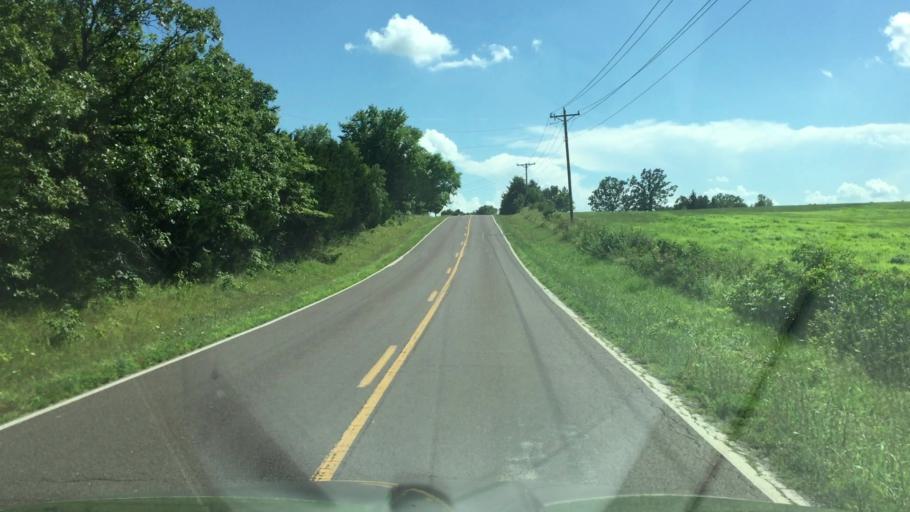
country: US
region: Missouri
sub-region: Miller County
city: Tuscumbia
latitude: 38.1222
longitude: -92.4680
